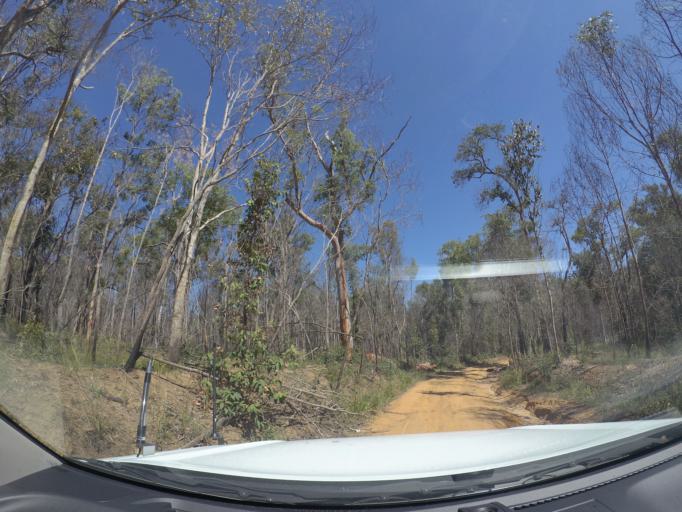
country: AU
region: Queensland
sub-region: Logan
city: North Maclean
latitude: -27.7793
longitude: 152.9367
